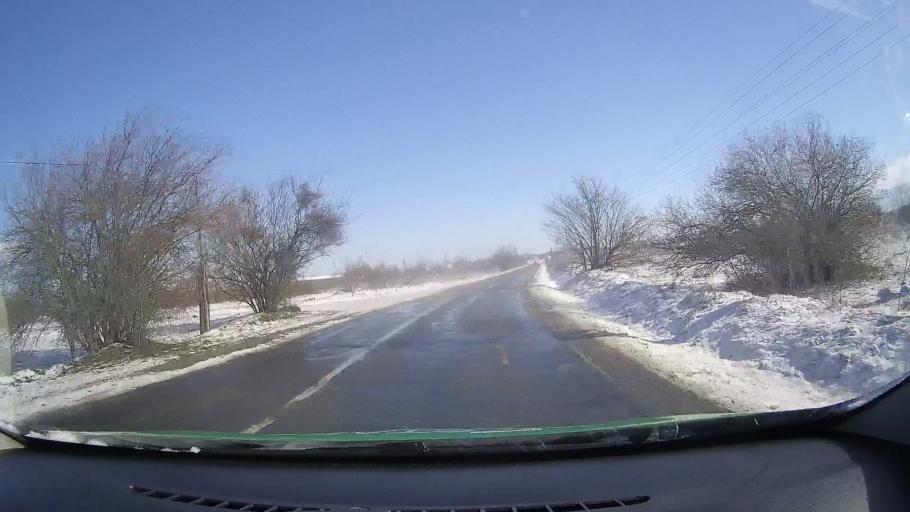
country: RO
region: Sibiu
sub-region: Comuna Racovita
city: Racovita
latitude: 45.6697
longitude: 24.3187
